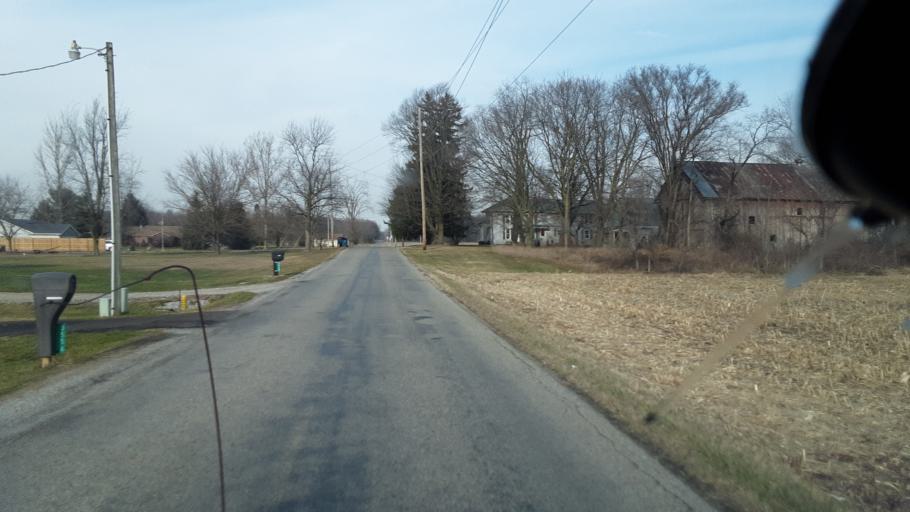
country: US
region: Indiana
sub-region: DeKalb County
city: Butler
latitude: 41.4046
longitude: -84.8893
